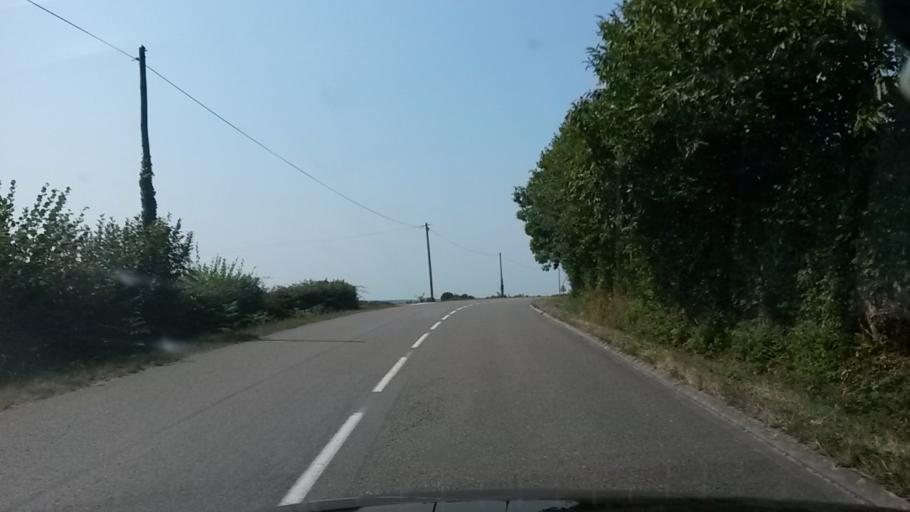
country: FR
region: Pays de la Loire
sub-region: Departement de la Mayenne
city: Courcite
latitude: 48.3590
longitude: -0.2153
